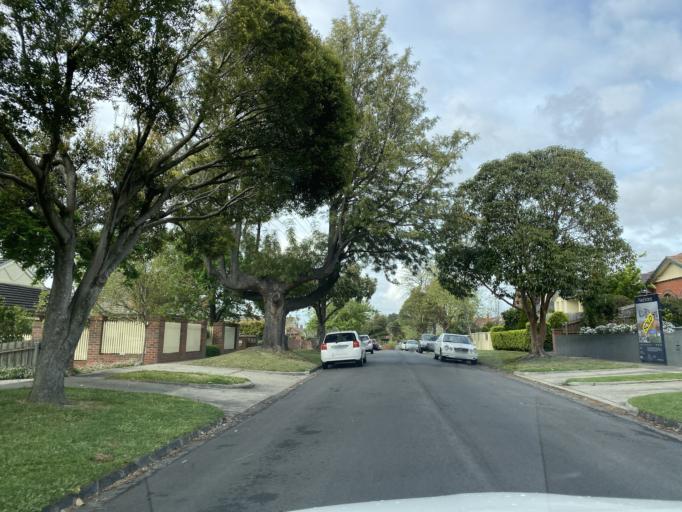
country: AU
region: Victoria
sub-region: Boroondara
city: Canterbury
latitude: -37.8331
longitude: 145.0901
